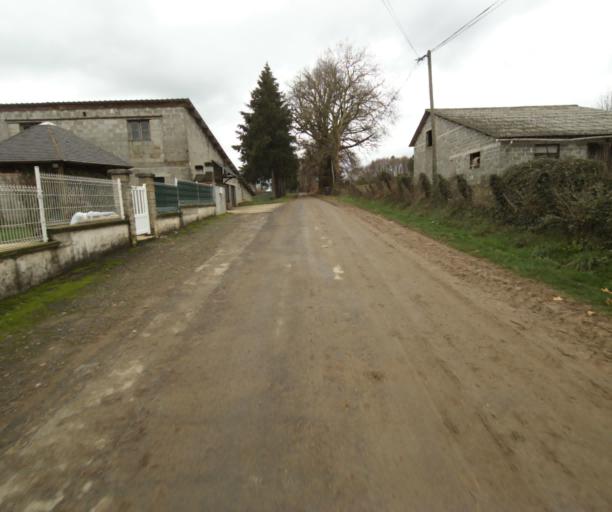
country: FR
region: Limousin
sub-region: Departement de la Correze
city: Saint-Mexant
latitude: 45.2728
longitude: 1.6181
